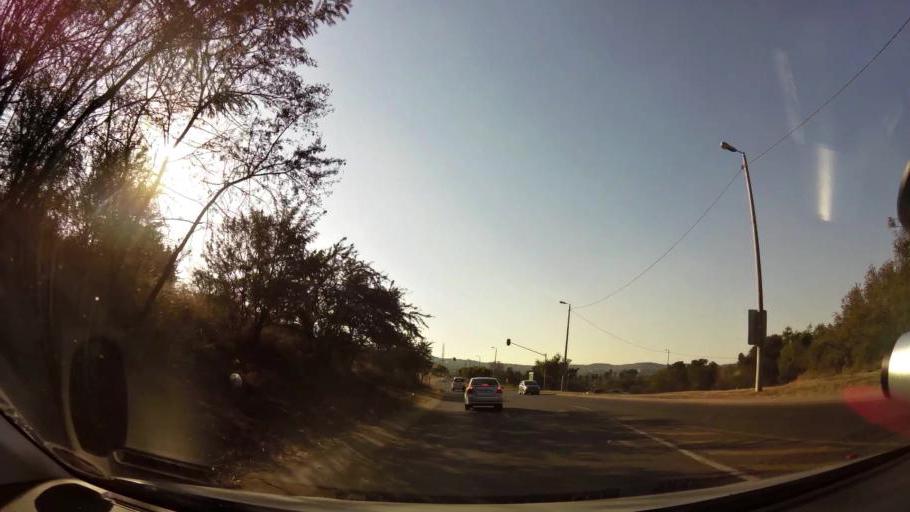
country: ZA
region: Gauteng
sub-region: City of Tshwane Metropolitan Municipality
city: Pretoria
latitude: -25.7547
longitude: 28.1335
